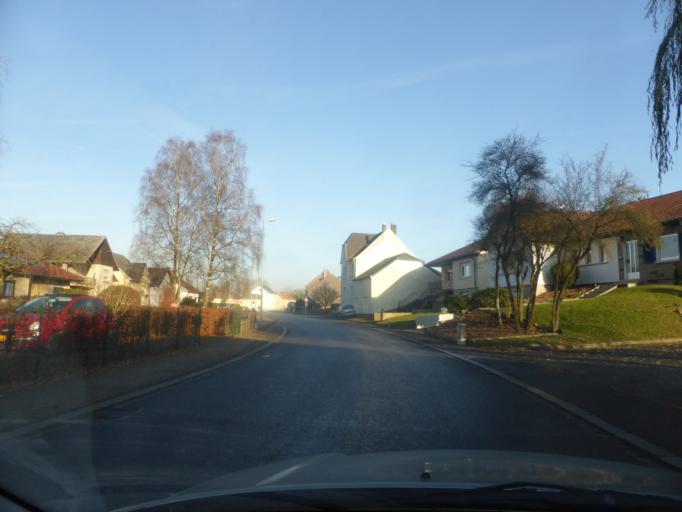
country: LU
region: Luxembourg
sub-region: Canton de Capellen
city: Garnich
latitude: 49.6088
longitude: 5.9435
